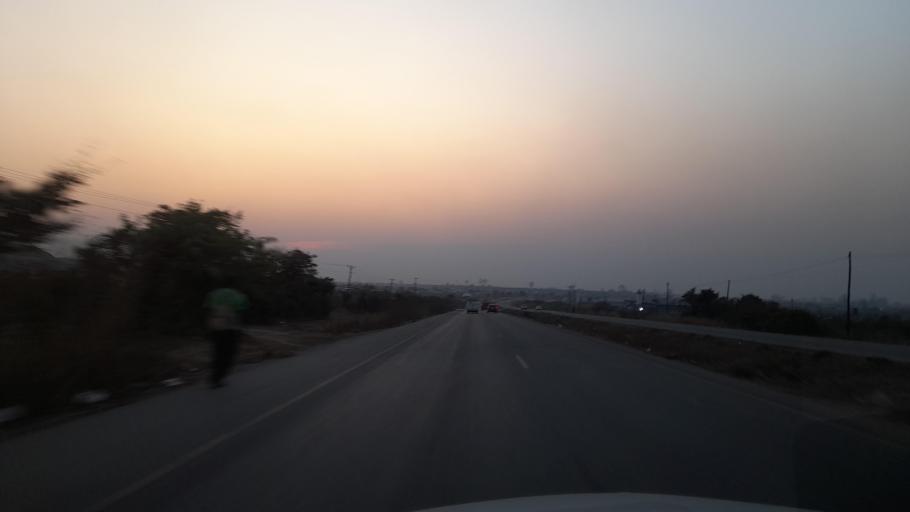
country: ZM
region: Copperbelt
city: Kitwe
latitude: -12.7659
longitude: 28.1747
